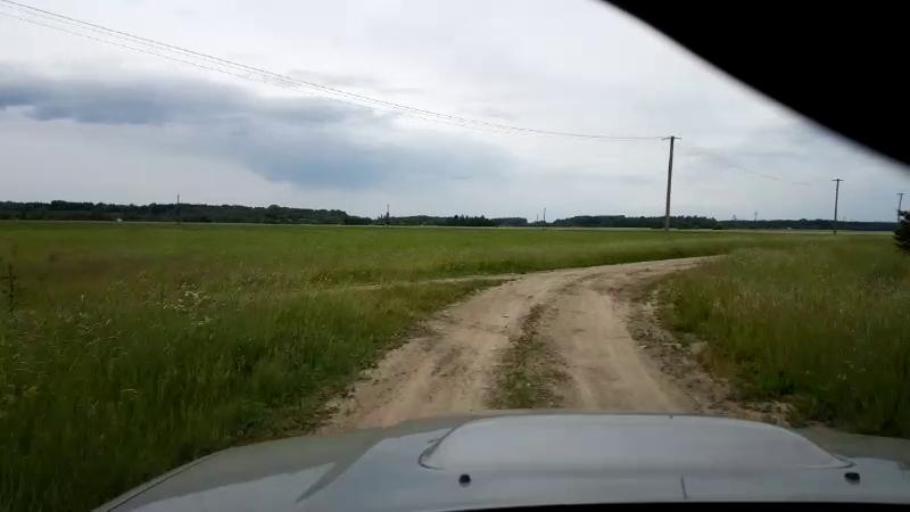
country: EE
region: Paernumaa
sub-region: Halinga vald
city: Parnu-Jaagupi
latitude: 58.5326
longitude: 24.6154
